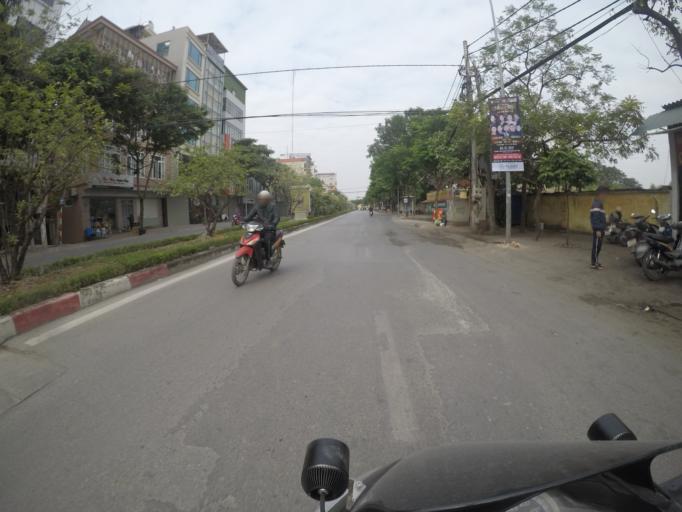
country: VN
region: Ha Noi
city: Tay Ho
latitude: 21.0653
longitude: 105.8102
